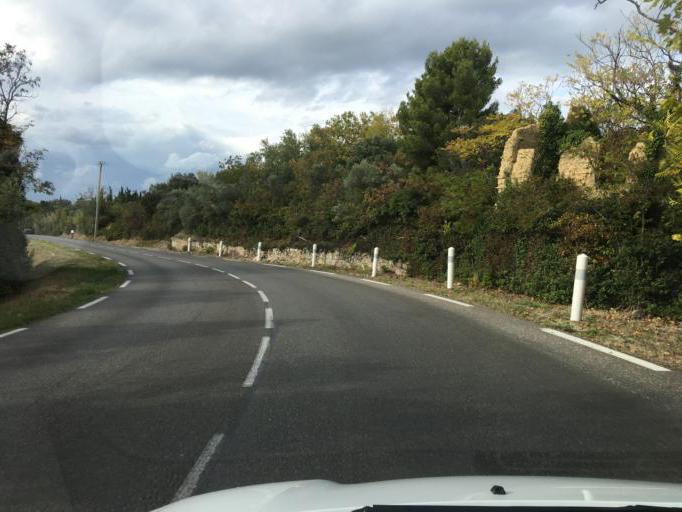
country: FR
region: Provence-Alpes-Cote d'Azur
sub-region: Departement du Vaucluse
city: Jonquerettes
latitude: 43.9344
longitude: 4.9220
